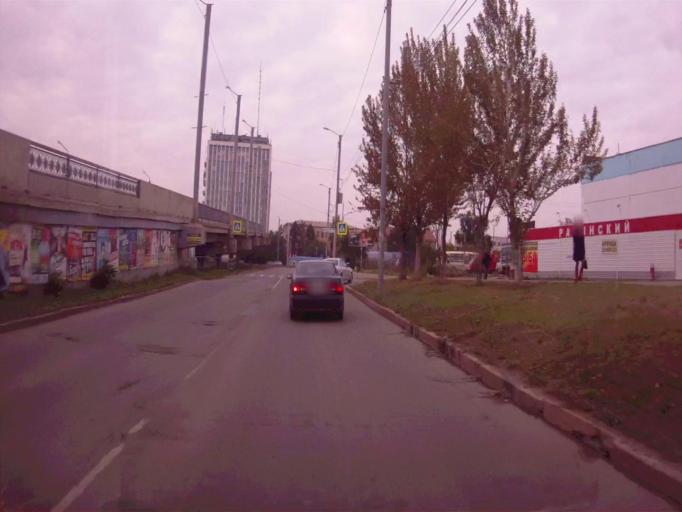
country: RU
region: Chelyabinsk
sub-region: Gorod Chelyabinsk
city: Chelyabinsk
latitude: 55.1386
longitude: 61.4104
